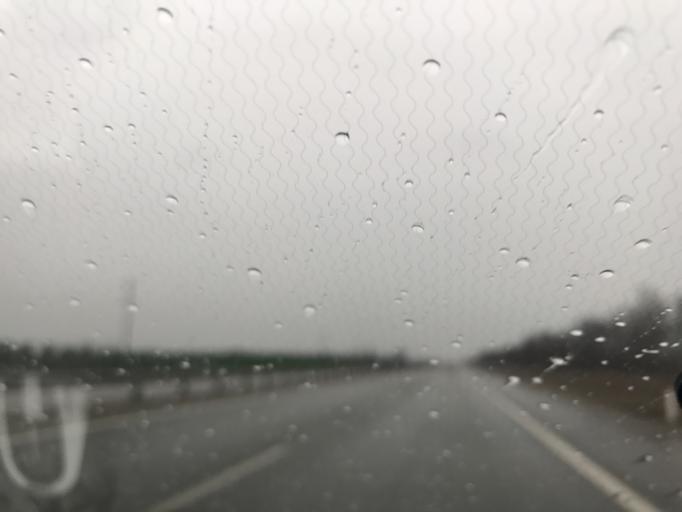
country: RU
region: Krasnodarskiy
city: Krylovskaya
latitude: 46.3148
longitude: 39.8028
